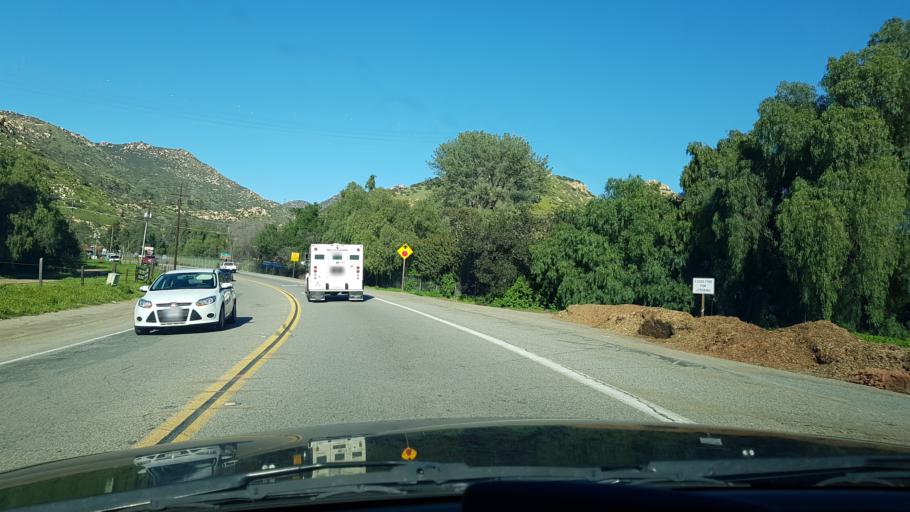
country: US
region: California
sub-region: San Diego County
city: Lakeside
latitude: 32.8733
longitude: -116.9111
